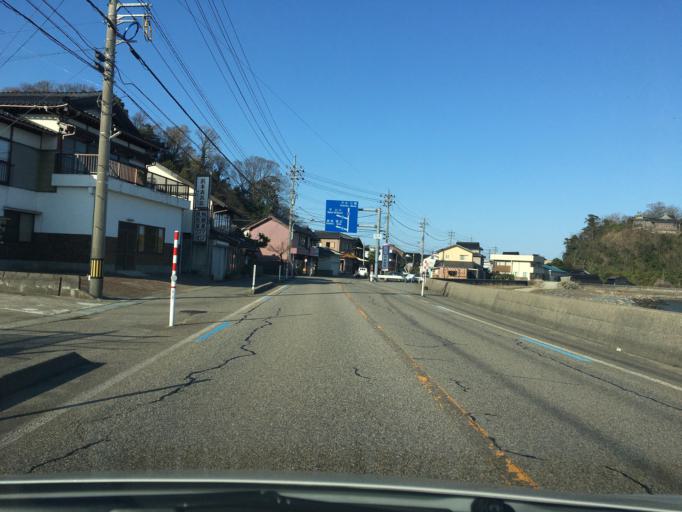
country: JP
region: Toyama
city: Himi
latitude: 36.8793
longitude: 136.9864
